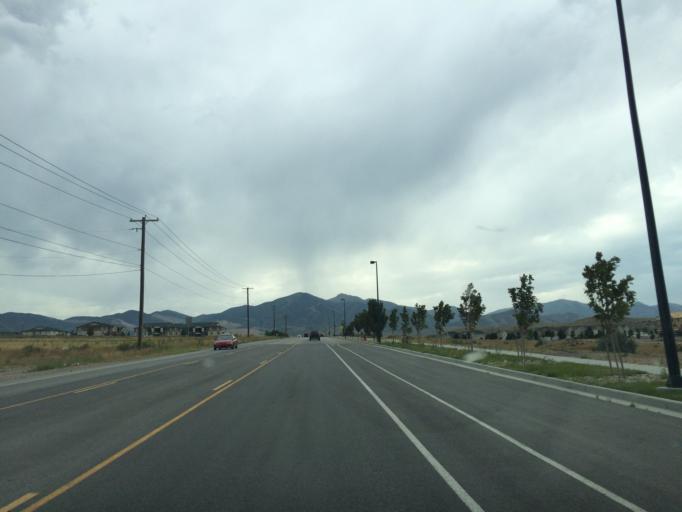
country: US
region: Utah
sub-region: Salt Lake County
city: Oquirrh
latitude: 40.6095
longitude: -112.0464
